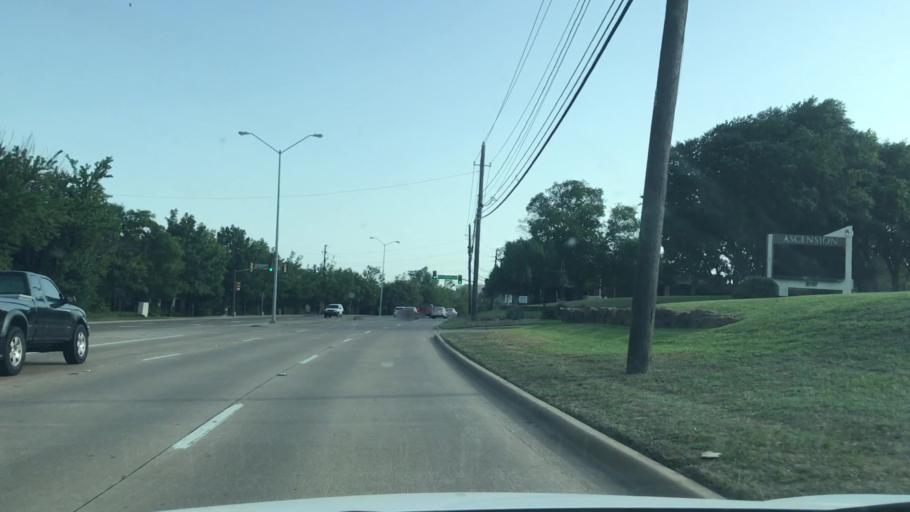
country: US
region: Texas
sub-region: Dallas County
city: Richardson
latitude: 32.8967
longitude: -96.7513
